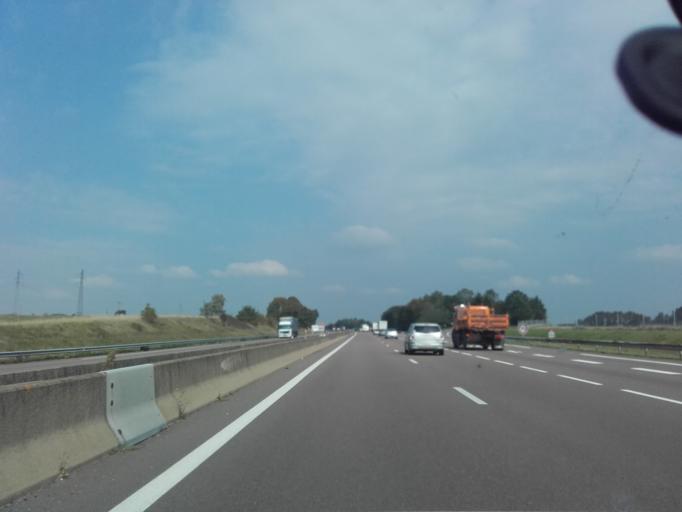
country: FR
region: Bourgogne
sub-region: Departement de Saone-et-Loire
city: Tournus
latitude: 46.5019
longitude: 4.9035
